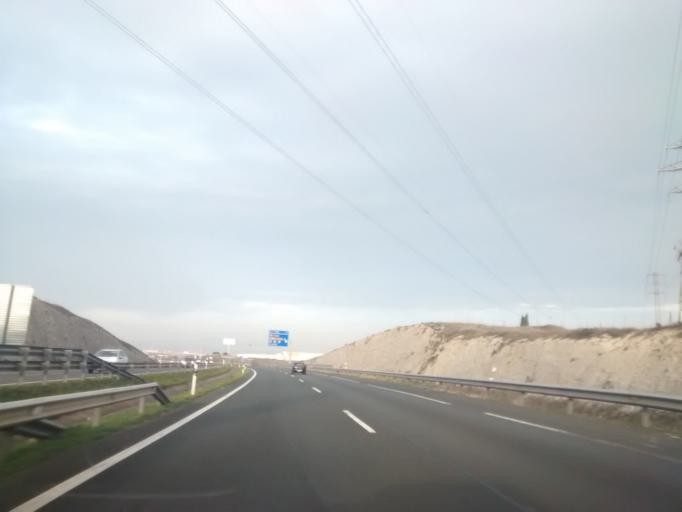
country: ES
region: Basque Country
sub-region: Provincia de Alava
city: Gasteiz / Vitoria
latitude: 42.8338
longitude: -2.7539
